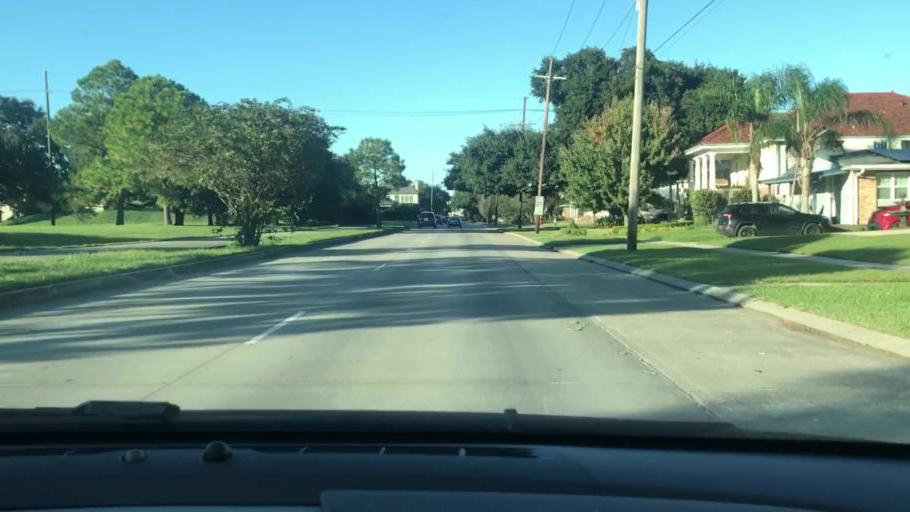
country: US
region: Louisiana
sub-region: Jefferson Parish
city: Metairie
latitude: 30.0159
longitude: -90.1138
